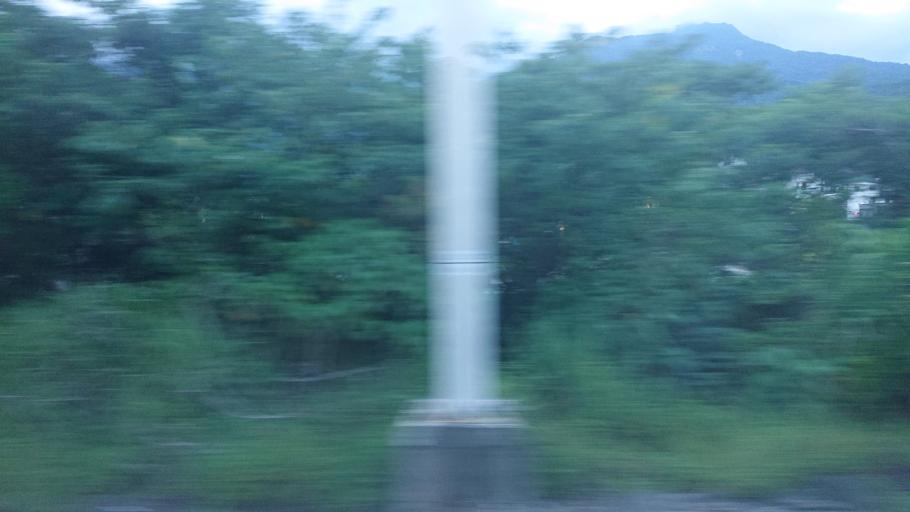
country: TW
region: Taiwan
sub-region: Taitung
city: Taitung
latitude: 23.0439
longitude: 121.1639
